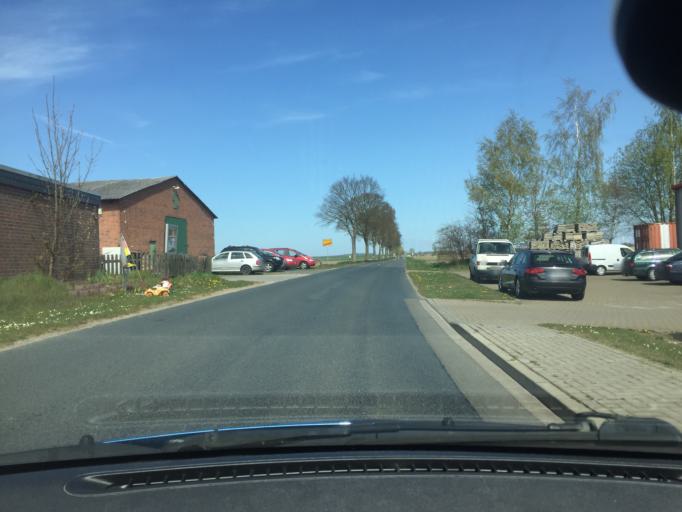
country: DE
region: Lower Saxony
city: Ratzlingen
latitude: 52.9779
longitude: 10.6748
